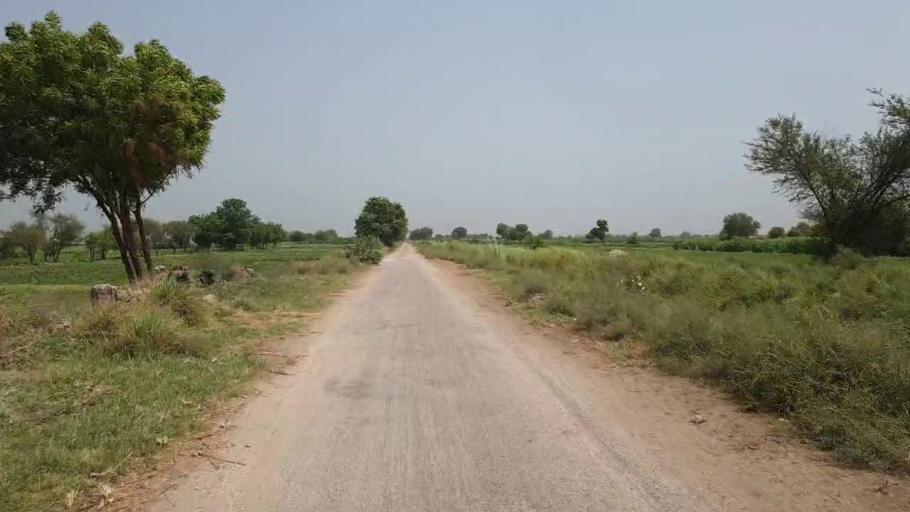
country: PK
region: Sindh
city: Nawabshah
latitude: 26.2773
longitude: 68.3132
